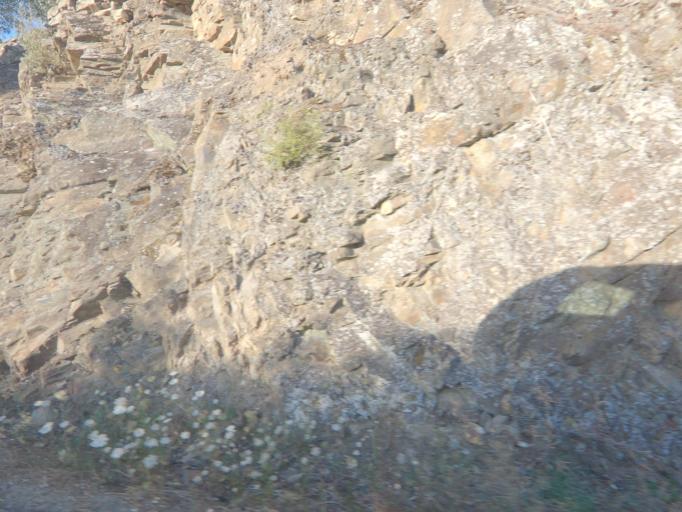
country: PT
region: Viseu
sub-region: Armamar
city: Armamar
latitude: 41.1765
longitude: -7.6905
